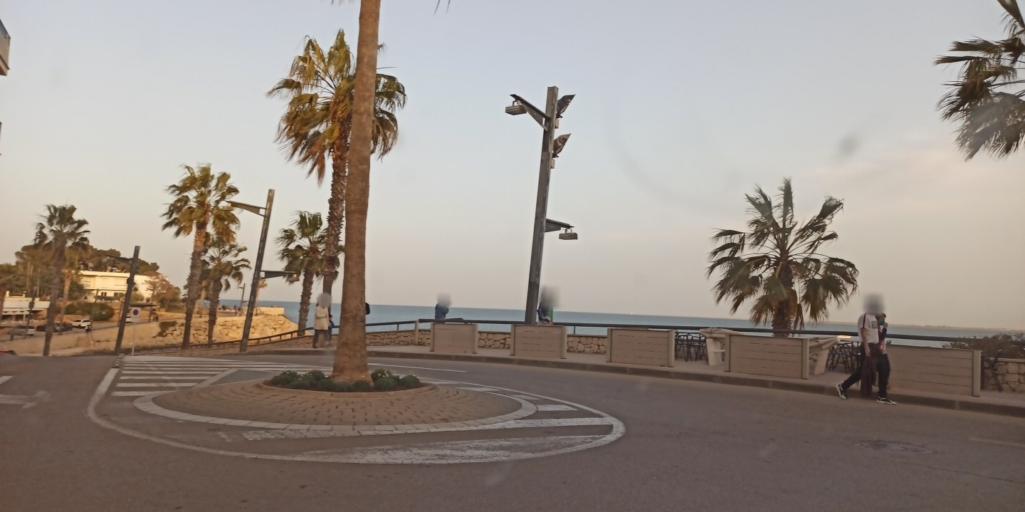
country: ES
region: Catalonia
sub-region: Provincia de Tarragona
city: L'Ampolla
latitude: 40.8128
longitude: 0.7140
